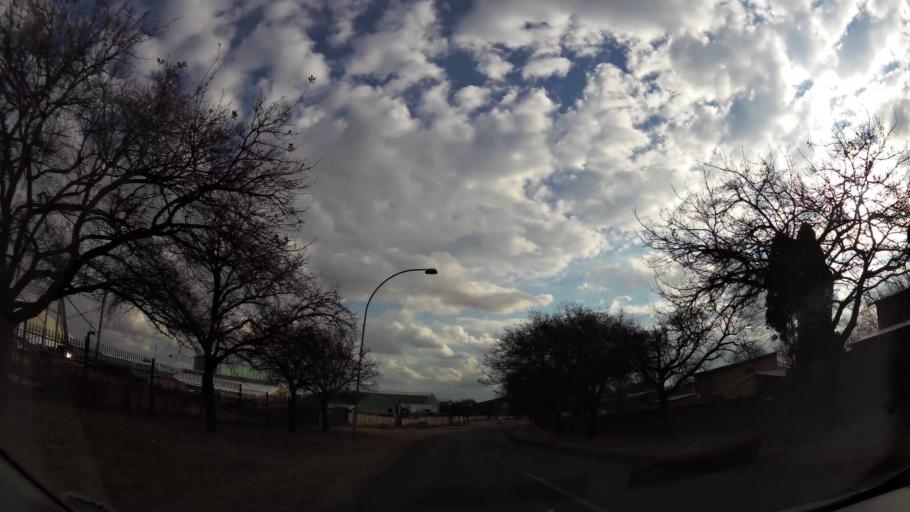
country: ZA
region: Orange Free State
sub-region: Fezile Dabi District Municipality
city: Sasolburg
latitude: -26.8264
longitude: 27.8270
